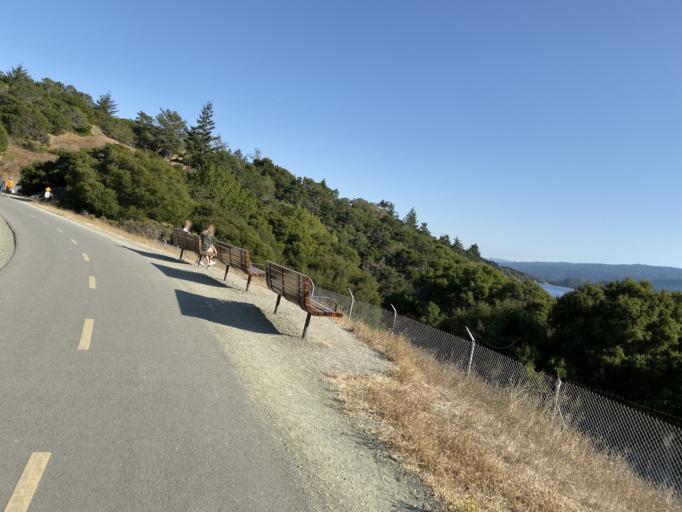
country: US
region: California
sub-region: San Mateo County
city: Highlands-Baywood Park
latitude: 37.5345
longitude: -122.3690
